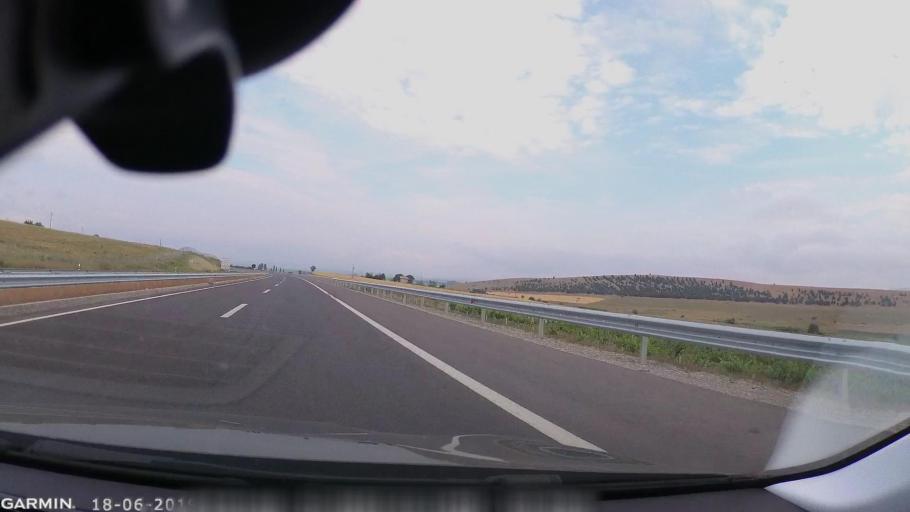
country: MK
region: Stip
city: Shtip
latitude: 41.7848
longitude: 22.1197
